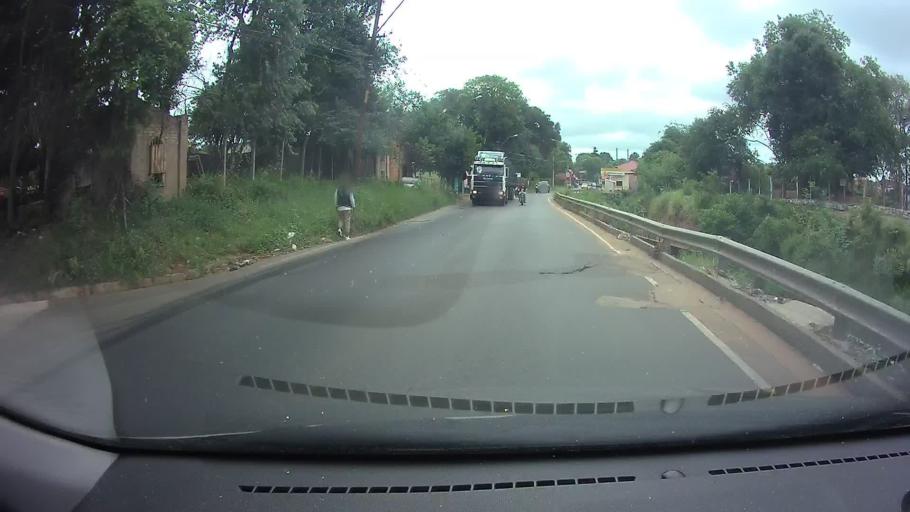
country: PY
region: Central
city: Nemby
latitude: -25.3786
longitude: -57.5457
